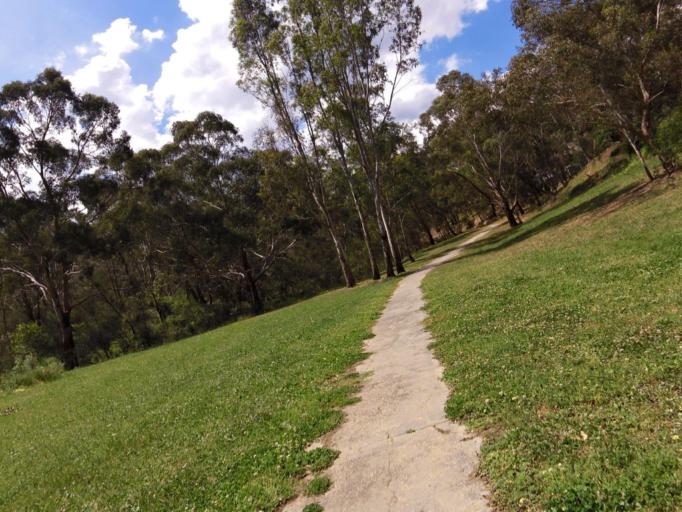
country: AU
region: Victoria
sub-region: Banyule
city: Greensborough
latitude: -37.6841
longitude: 145.1029
